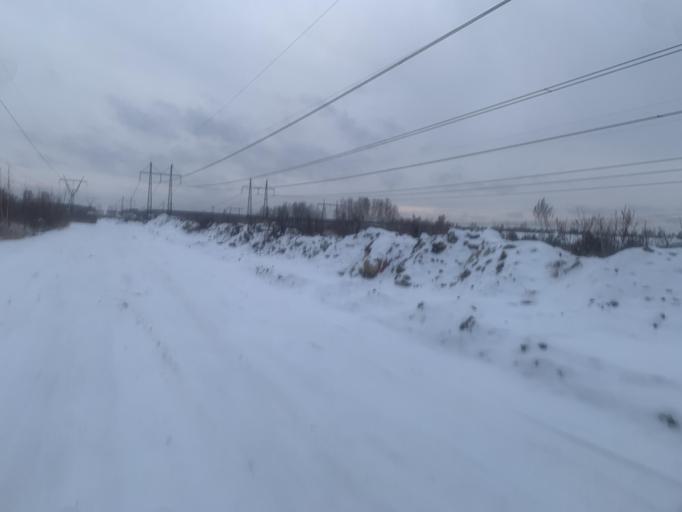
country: RU
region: Chelyabinsk
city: Roshchino
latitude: 55.1910
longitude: 61.2590
